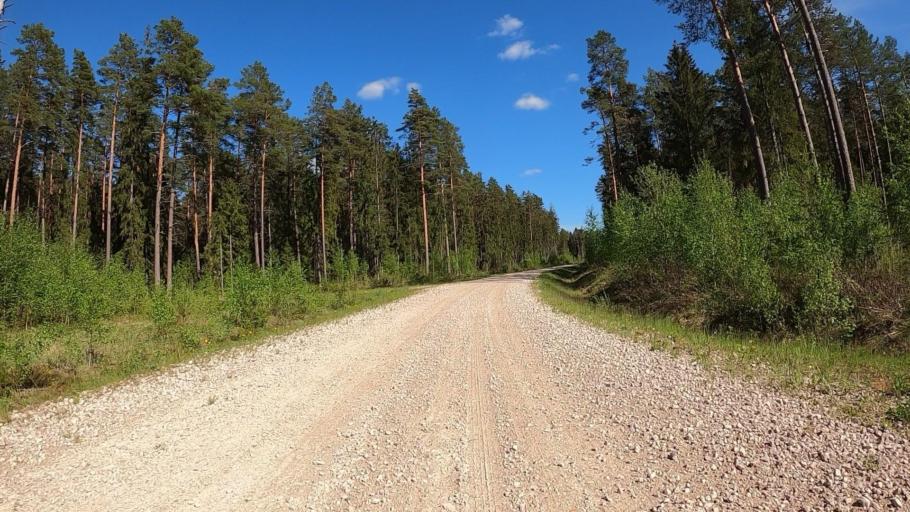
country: LV
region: Baldone
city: Baldone
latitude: 56.7838
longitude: 24.3451
